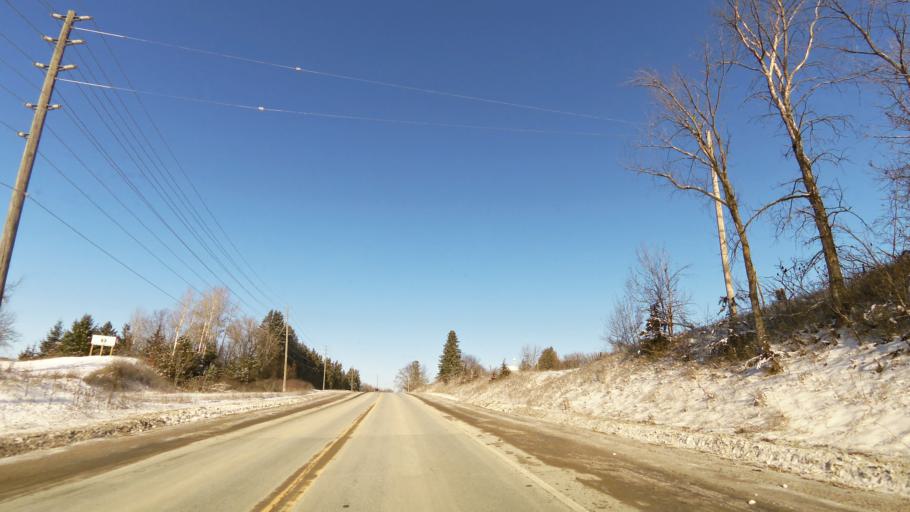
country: CA
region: Ontario
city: Quinte West
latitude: 44.1999
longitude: -77.8189
